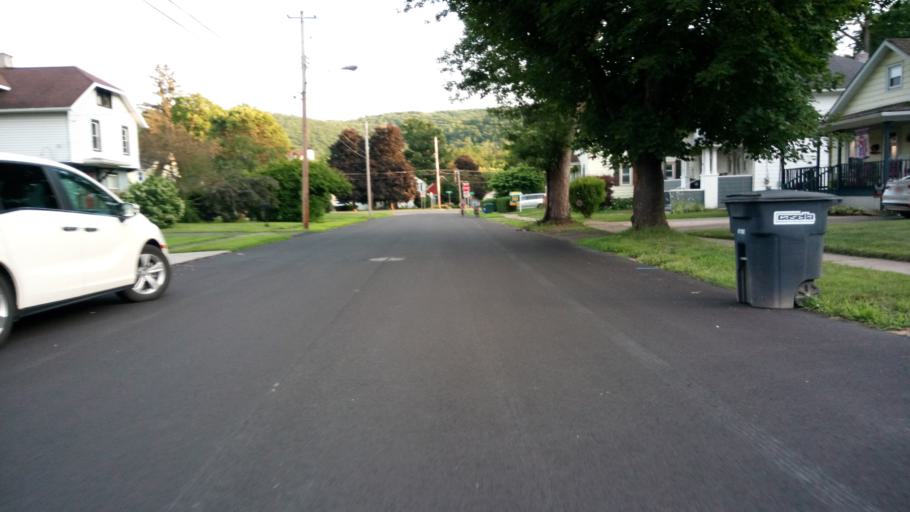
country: US
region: New York
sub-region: Chemung County
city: West Elmira
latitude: 42.0786
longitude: -76.8512
